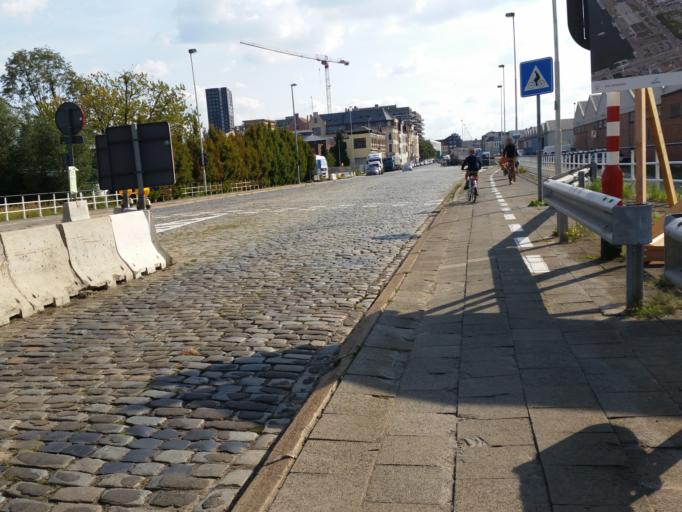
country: BE
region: Flanders
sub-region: Provincie Antwerpen
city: Antwerpen
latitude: 51.2365
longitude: 4.4090
